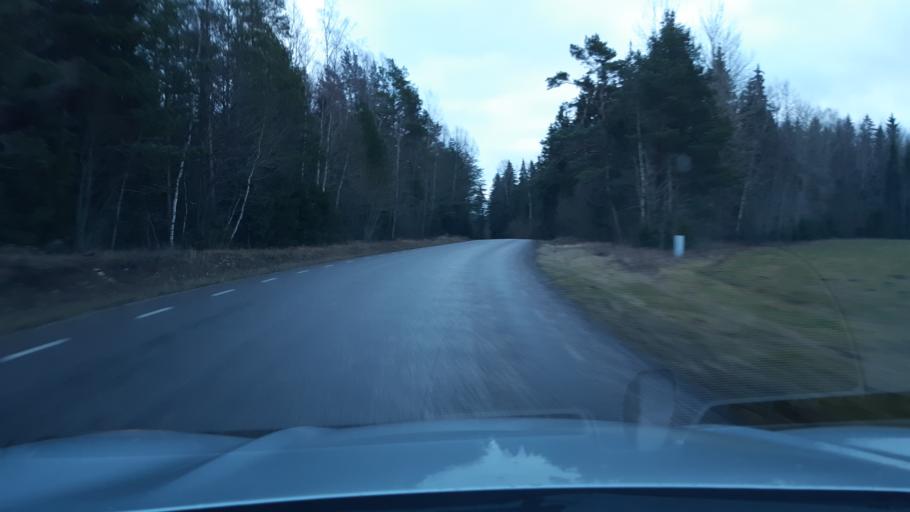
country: EE
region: Harju
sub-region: Saue linn
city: Saue
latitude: 59.2183
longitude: 24.5474
